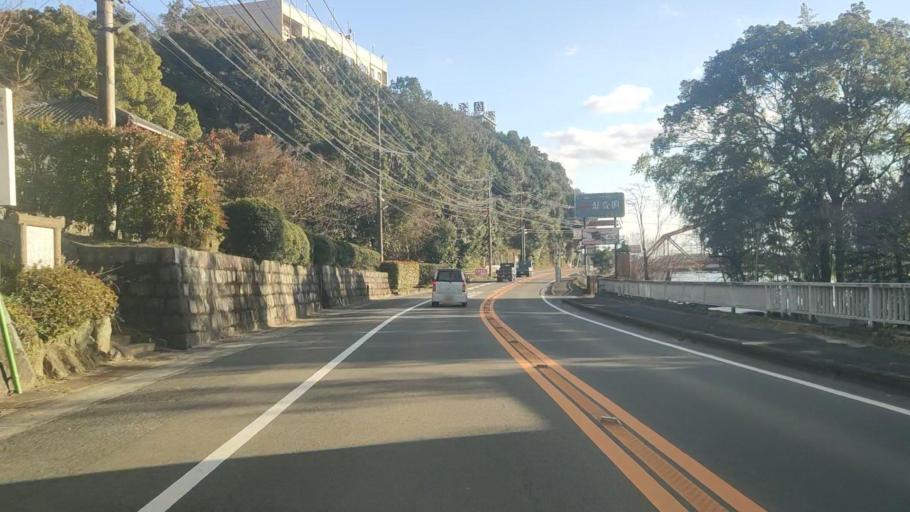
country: JP
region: Saga Prefecture
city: Saga-shi
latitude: 33.3285
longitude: 130.2687
